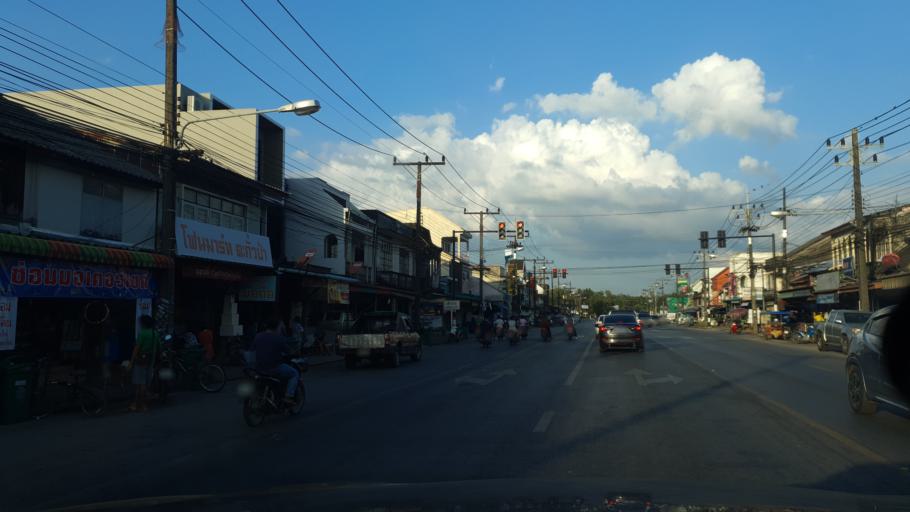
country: TH
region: Phangnga
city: Takua Pa
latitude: 8.8429
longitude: 98.2880
